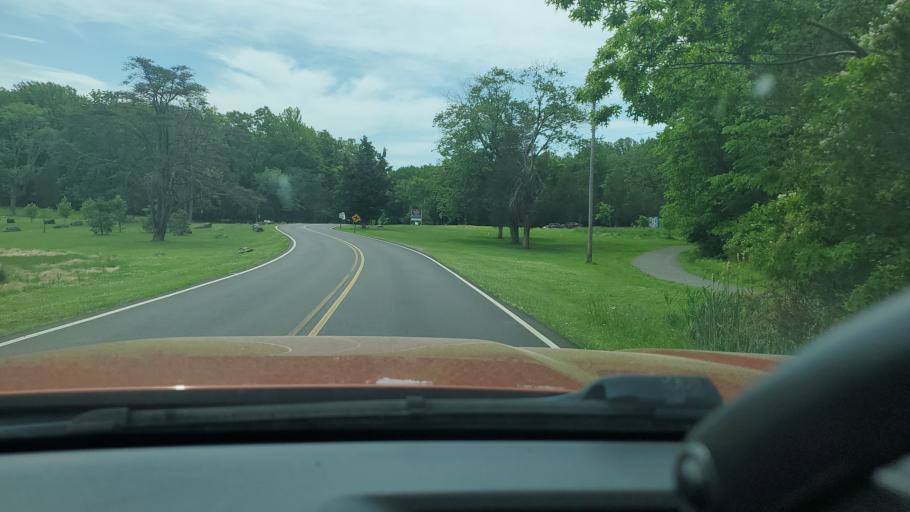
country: US
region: Pennsylvania
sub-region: Montgomery County
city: Red Hill
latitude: 40.3316
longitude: -75.4873
